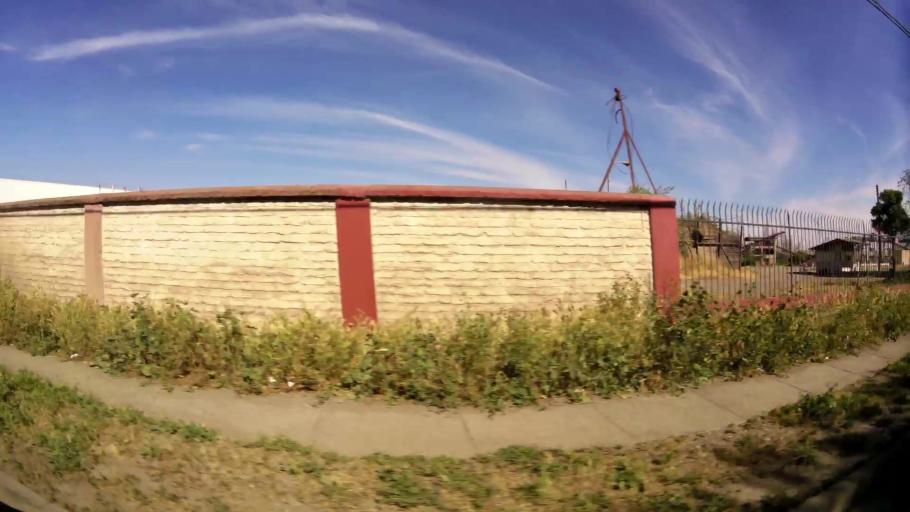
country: CL
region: Santiago Metropolitan
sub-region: Provincia de Santiago
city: Lo Prado
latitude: -33.4839
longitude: -70.7081
